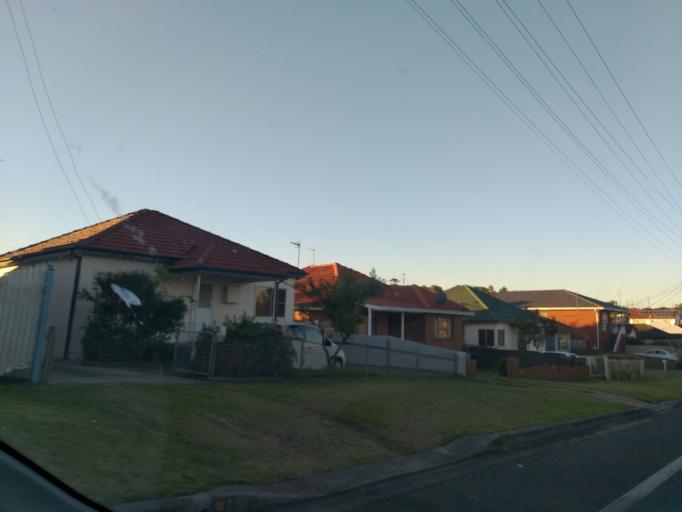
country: AU
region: New South Wales
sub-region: Wollongong
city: Port Kembla
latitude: -34.4891
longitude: 150.8960
